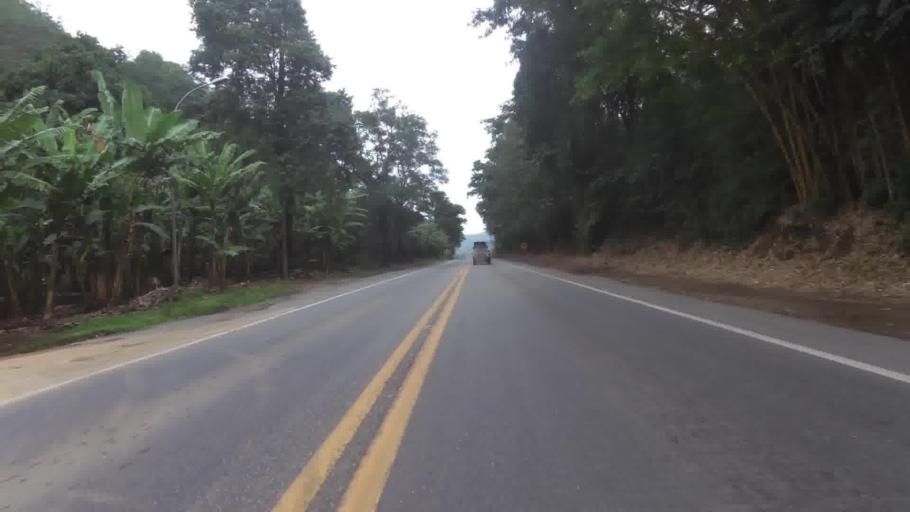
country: BR
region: Espirito Santo
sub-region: Iconha
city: Iconha
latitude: -20.7968
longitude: -40.8206
